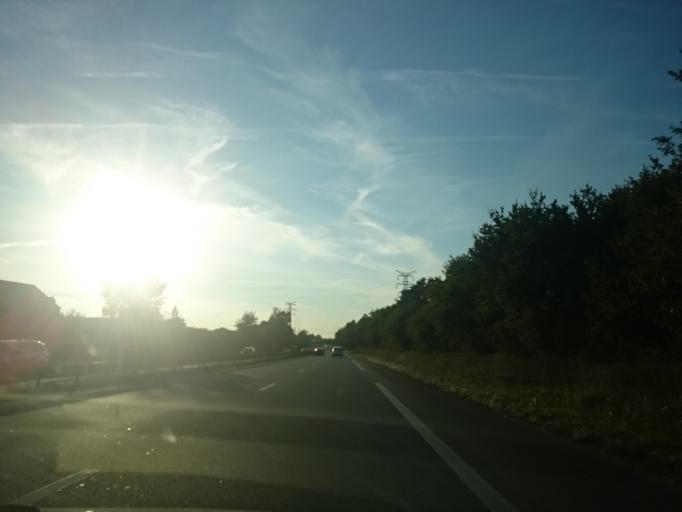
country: FR
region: Brittany
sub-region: Departement du Morbihan
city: Vannes
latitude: 47.6684
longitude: -2.7352
